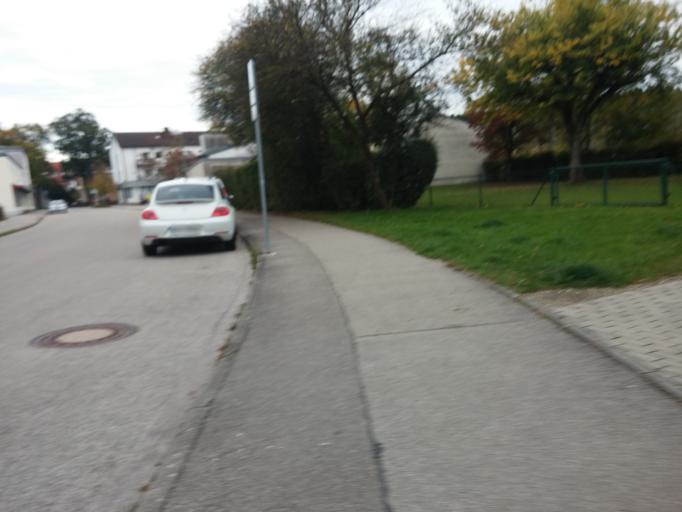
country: DE
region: Bavaria
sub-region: Upper Bavaria
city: Kirchseeon
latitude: 48.0725
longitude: 11.8866
